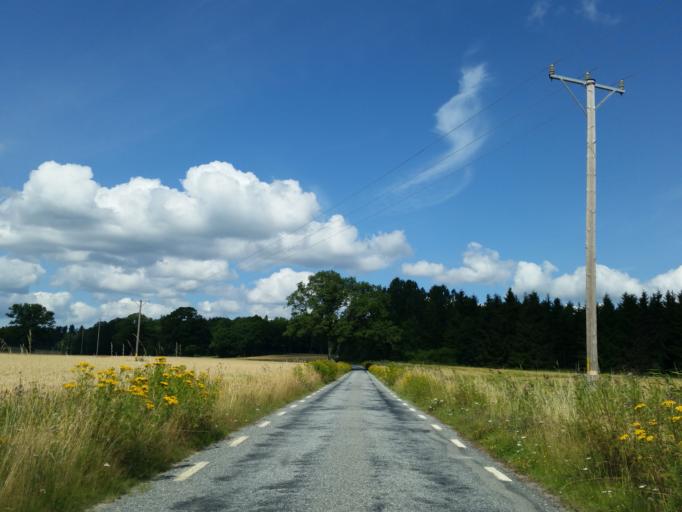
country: SE
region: Stockholm
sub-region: Sodertalje Kommun
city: Pershagen
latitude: 59.0495
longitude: 17.6594
